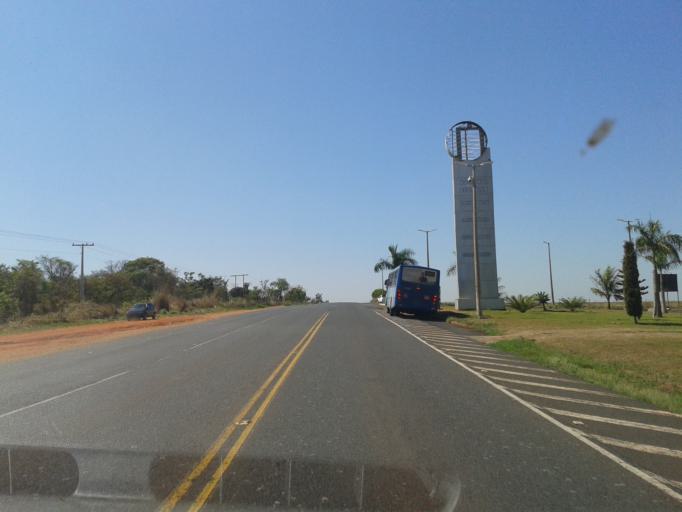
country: BR
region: Minas Gerais
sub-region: Uberlandia
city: Uberlandia
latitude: -19.0998
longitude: -47.9897
